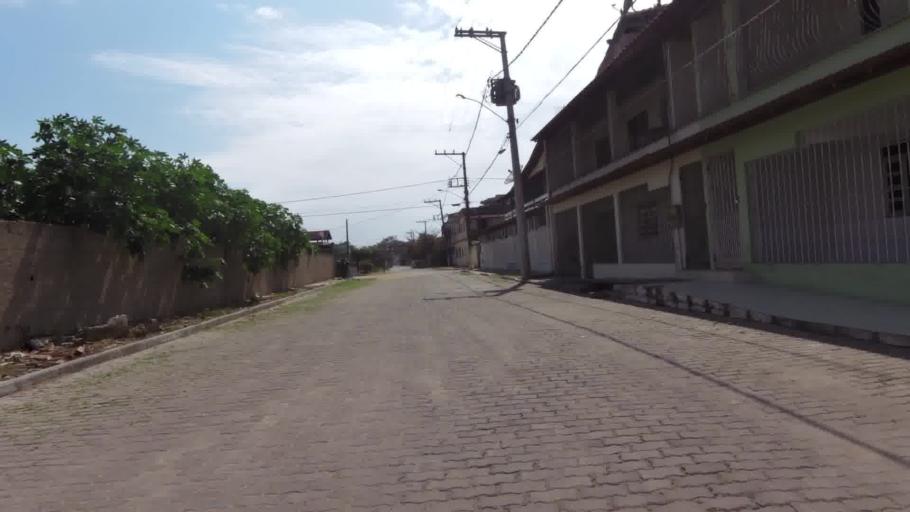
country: BR
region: Espirito Santo
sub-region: Marataizes
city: Marataizes
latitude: -21.0302
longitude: -40.8147
